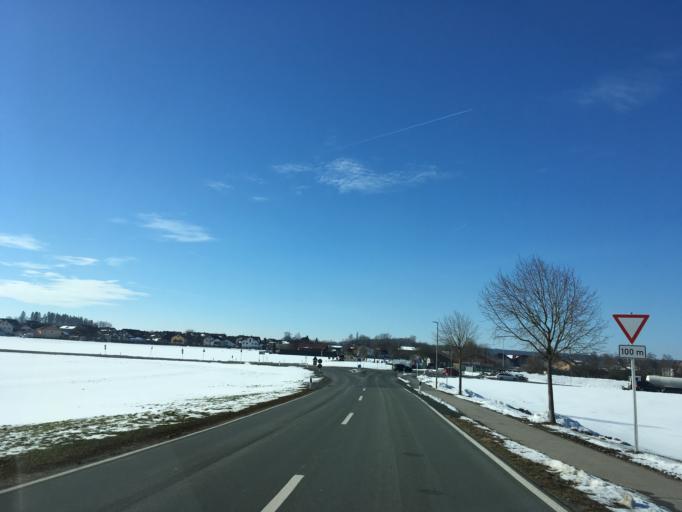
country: DE
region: Bavaria
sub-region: Upper Bavaria
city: Albaching
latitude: 48.1111
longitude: 12.1209
